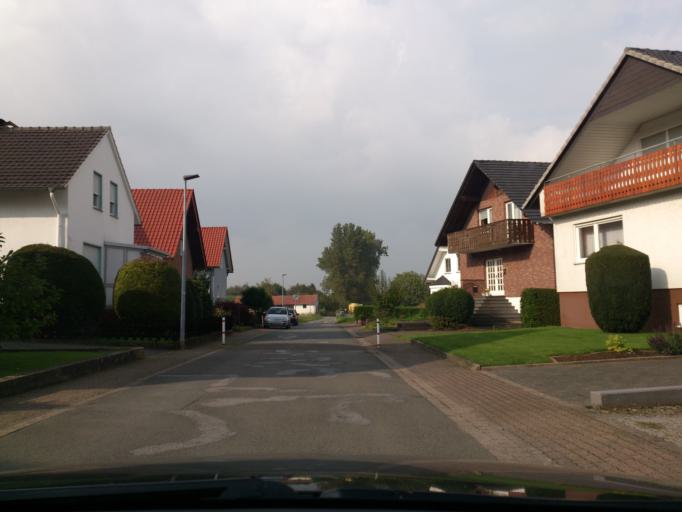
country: DE
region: North Rhine-Westphalia
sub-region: Regierungsbezirk Detmold
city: Willebadessen
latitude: 51.5794
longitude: 9.0343
